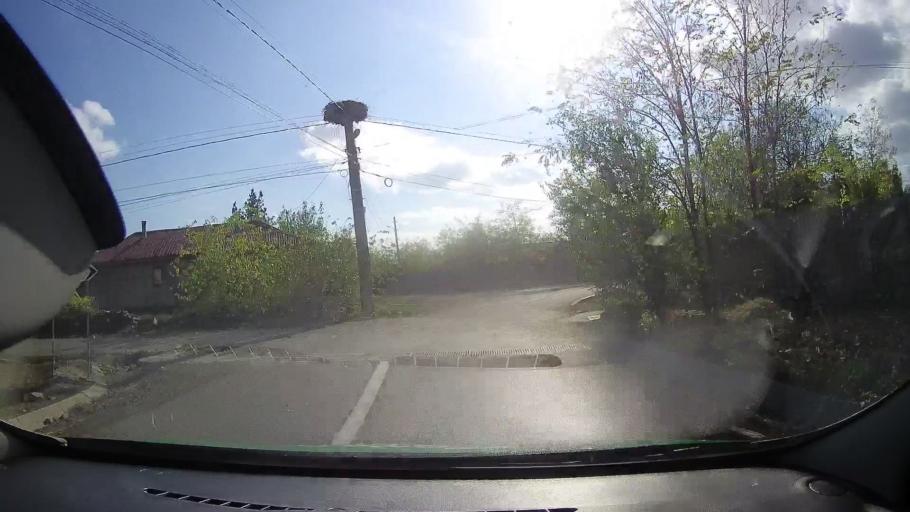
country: RO
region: Constanta
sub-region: Comuna Istria
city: Istria
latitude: 44.5735
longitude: 28.7142
